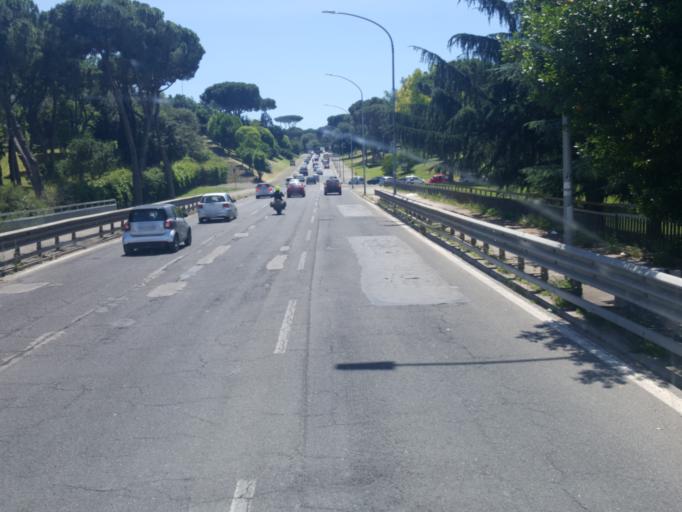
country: IT
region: Latium
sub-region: Citta metropolitana di Roma Capitale
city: Selcetta
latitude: 41.8283
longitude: 12.4662
